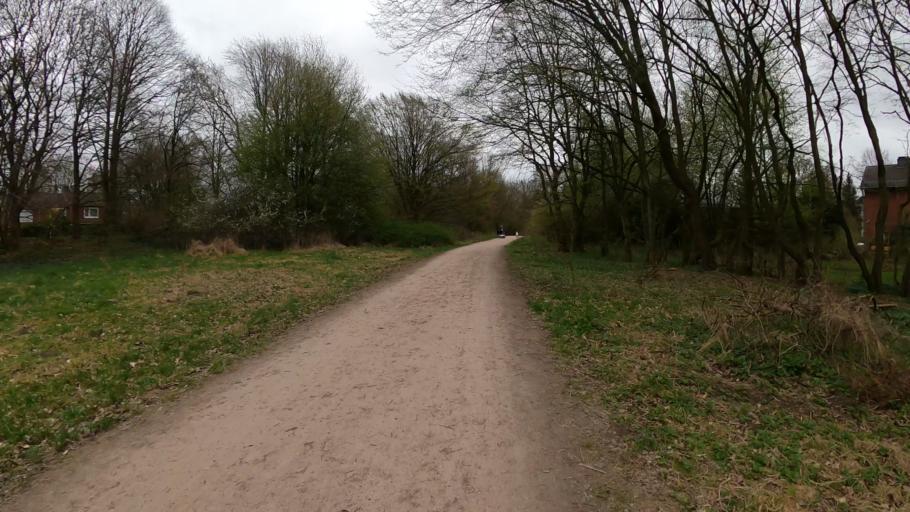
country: DE
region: Hamburg
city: Langenhorn
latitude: 53.6534
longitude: 9.9992
